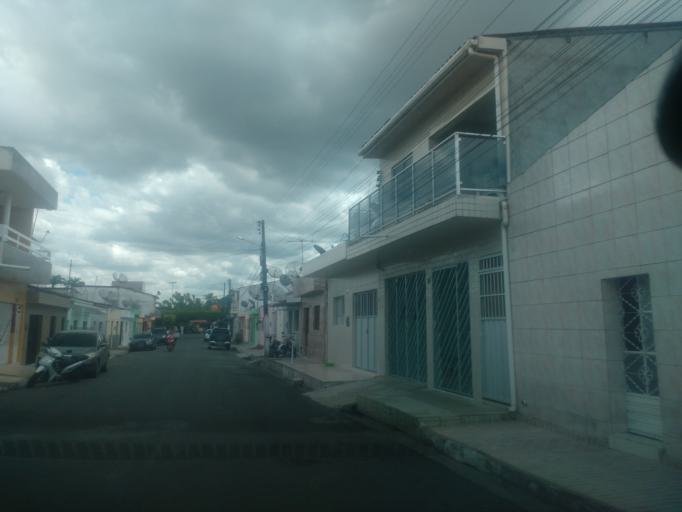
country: BR
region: Alagoas
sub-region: Uniao Dos Palmares
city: Uniao dos Palmares
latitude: -9.1562
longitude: -36.0286
